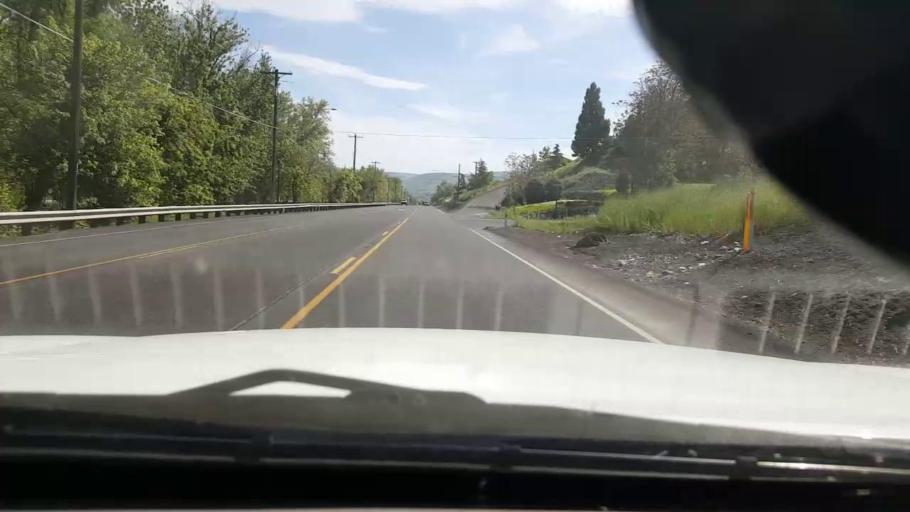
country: US
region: Washington
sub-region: Asotin County
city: West Clarkston-Highland
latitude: 46.3889
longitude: -117.0478
